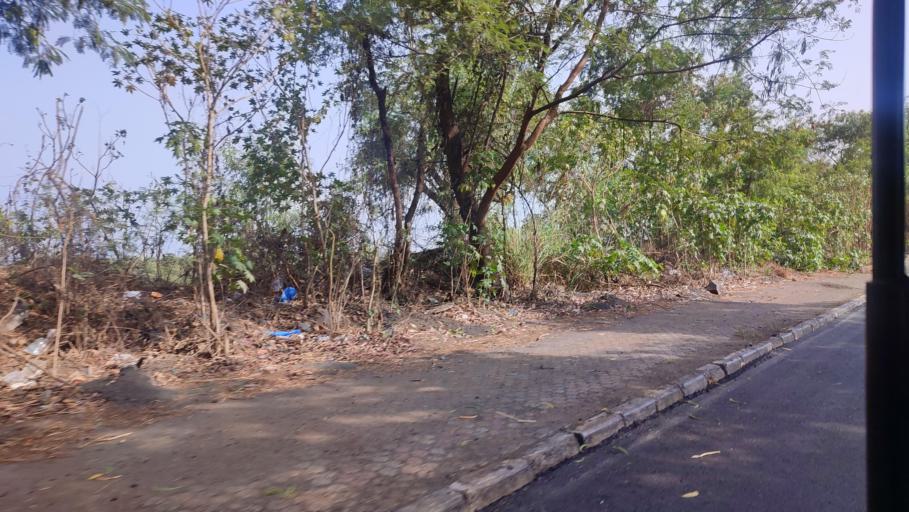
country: IN
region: Maharashtra
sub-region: Mumbai Suburban
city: Powai
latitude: 19.1315
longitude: 72.9429
